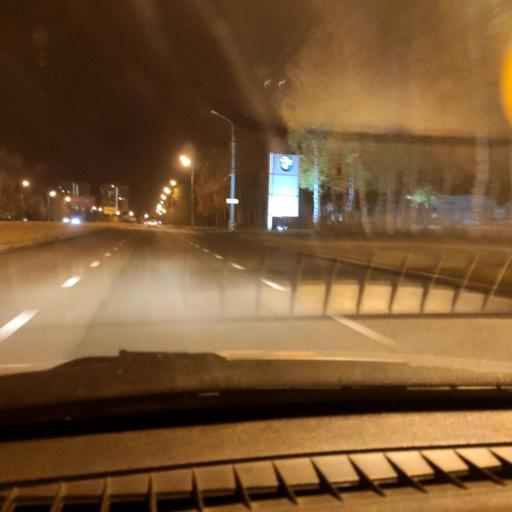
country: RU
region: Samara
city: Tol'yatti
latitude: 53.5022
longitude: 49.2629
